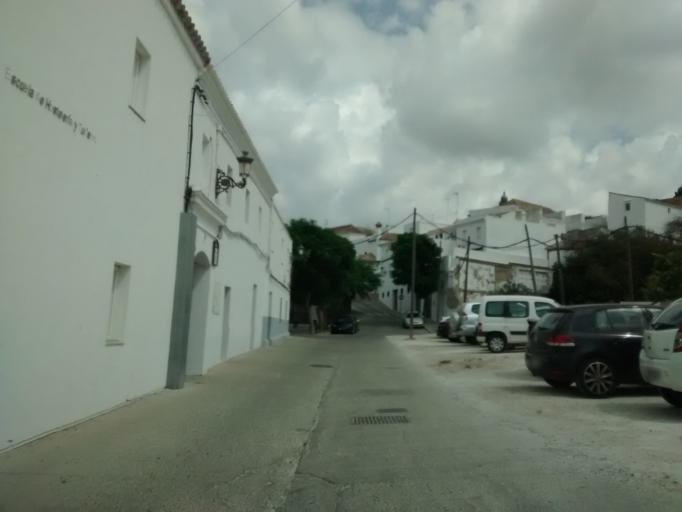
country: ES
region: Andalusia
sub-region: Provincia de Cadiz
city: Medina Sidonia
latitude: 36.4550
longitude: -5.9286
